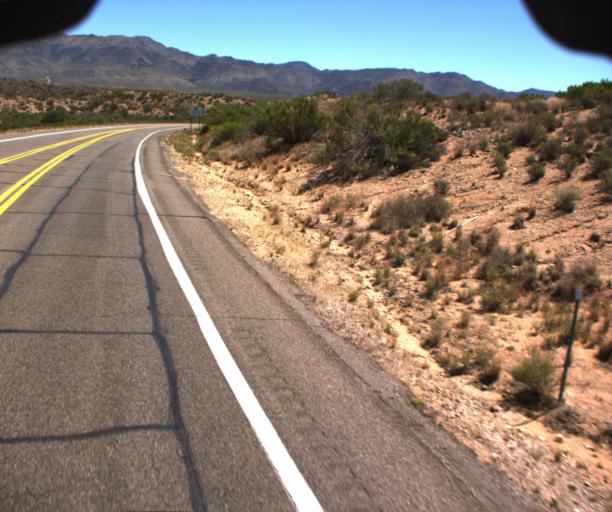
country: US
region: Arizona
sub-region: Yavapai County
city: Congress
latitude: 34.1641
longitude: -112.8432
